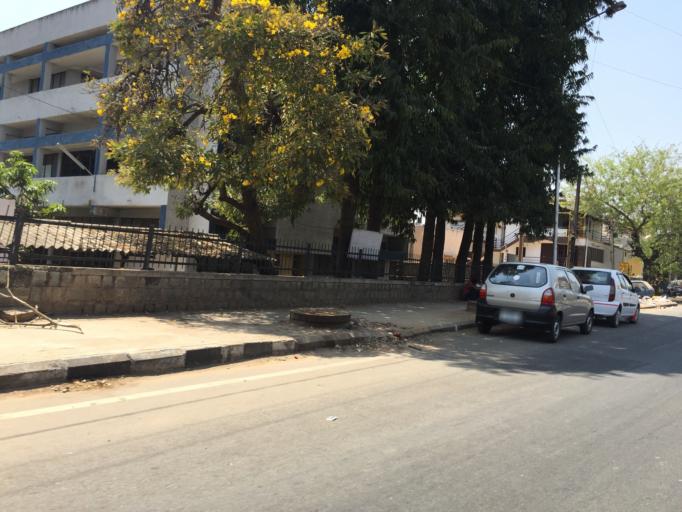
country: IN
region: Karnataka
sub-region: Bangalore Urban
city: Bangalore
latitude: 12.9820
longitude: 77.6266
